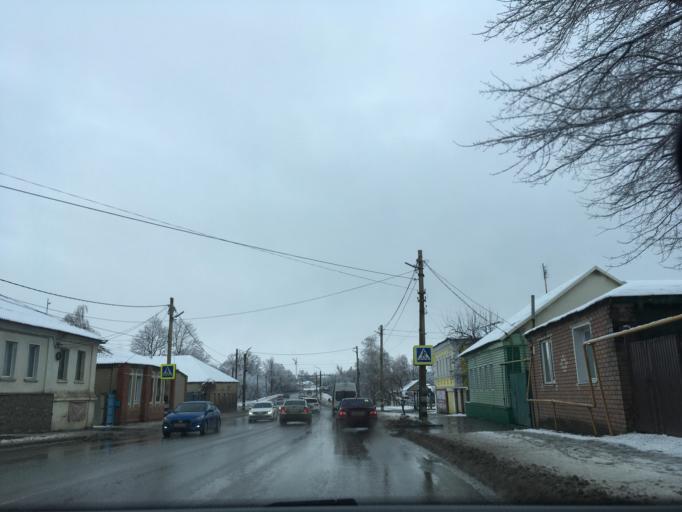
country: RU
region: Voronezj
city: Rossosh'
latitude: 50.1993
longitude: 39.5466
